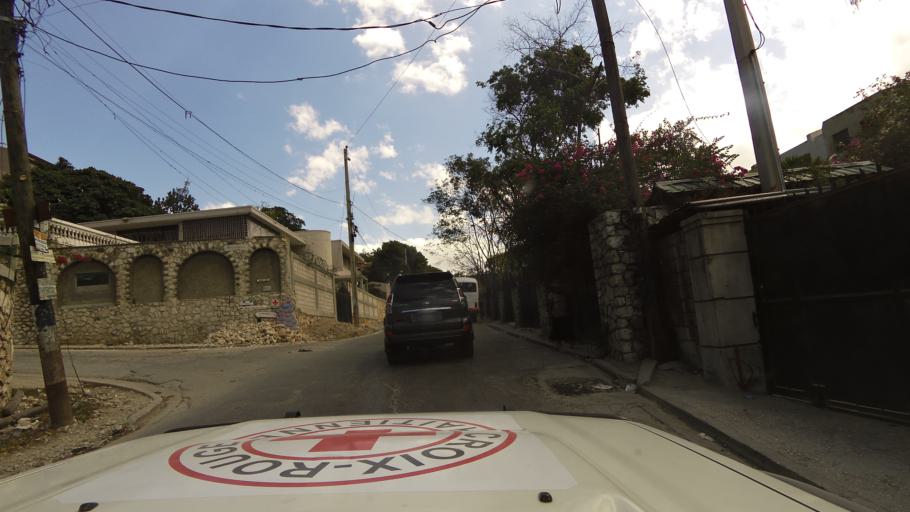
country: HT
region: Ouest
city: Delmas 73
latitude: 18.5301
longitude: -72.2933
